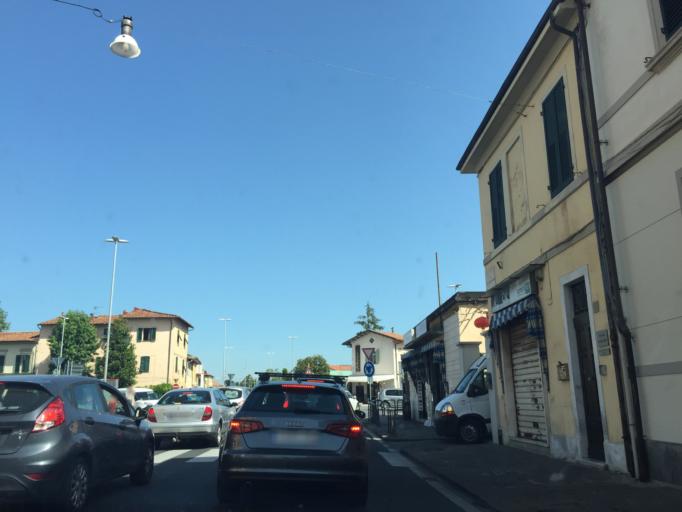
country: IT
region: Tuscany
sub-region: Province of Pisa
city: Pisa
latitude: 43.7245
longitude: 10.3915
